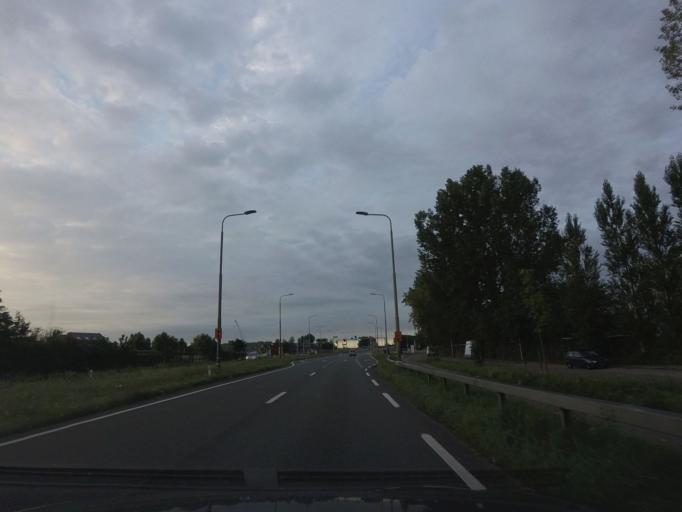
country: NL
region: North Holland
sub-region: Gemeente Zaanstad
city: Zaanstad
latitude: 52.4989
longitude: 4.7773
